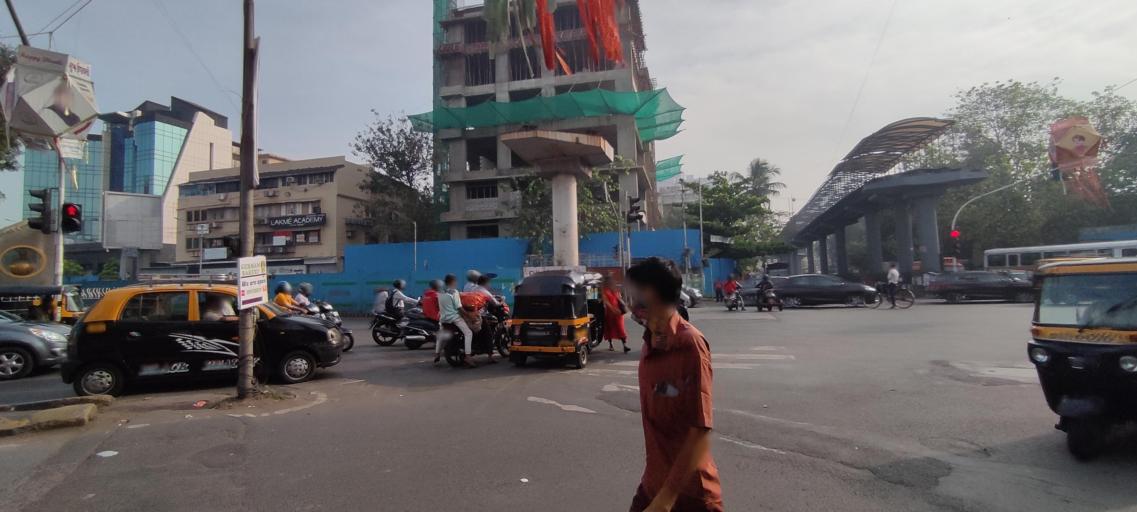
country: IN
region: Maharashtra
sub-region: Mumbai Suburban
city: Mumbai
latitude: 19.0542
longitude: 72.8376
